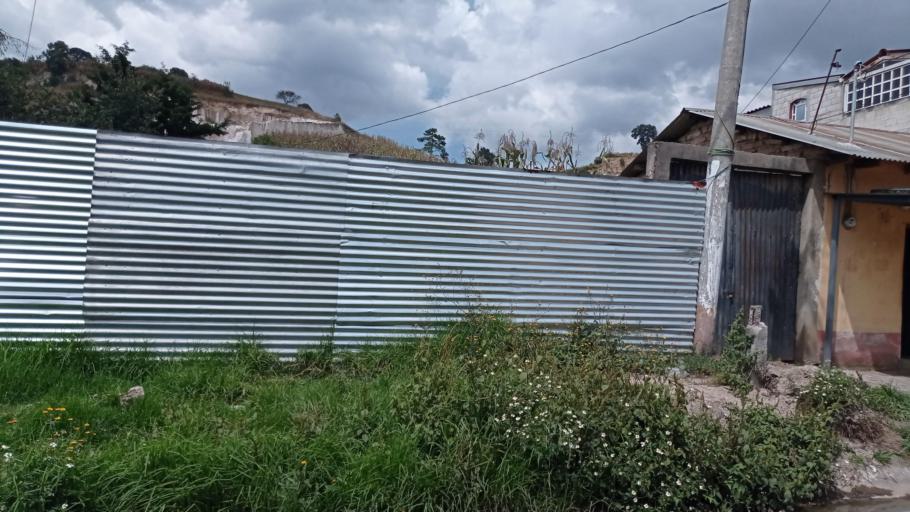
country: GT
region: Quetzaltenango
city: Quetzaltenango
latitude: 14.8523
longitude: -91.4953
